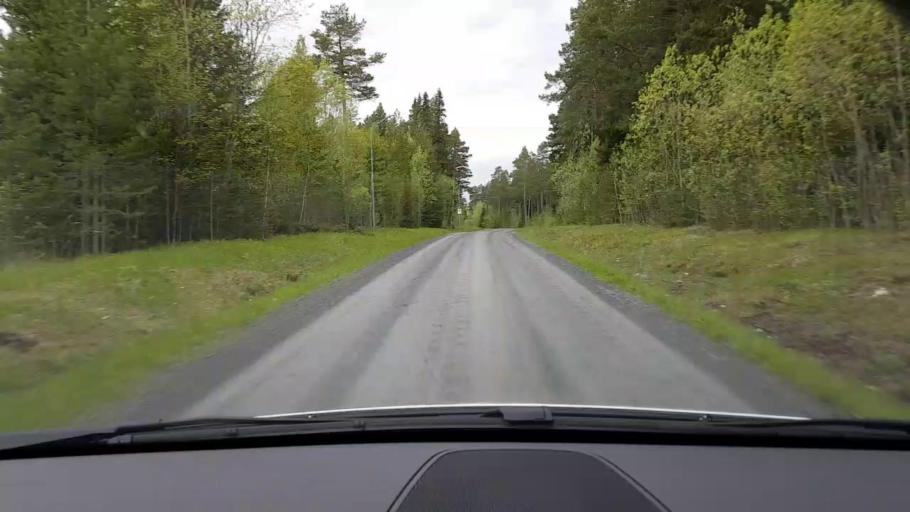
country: SE
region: Jaemtland
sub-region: Krokoms Kommun
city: Valla
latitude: 63.3022
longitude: 14.0225
